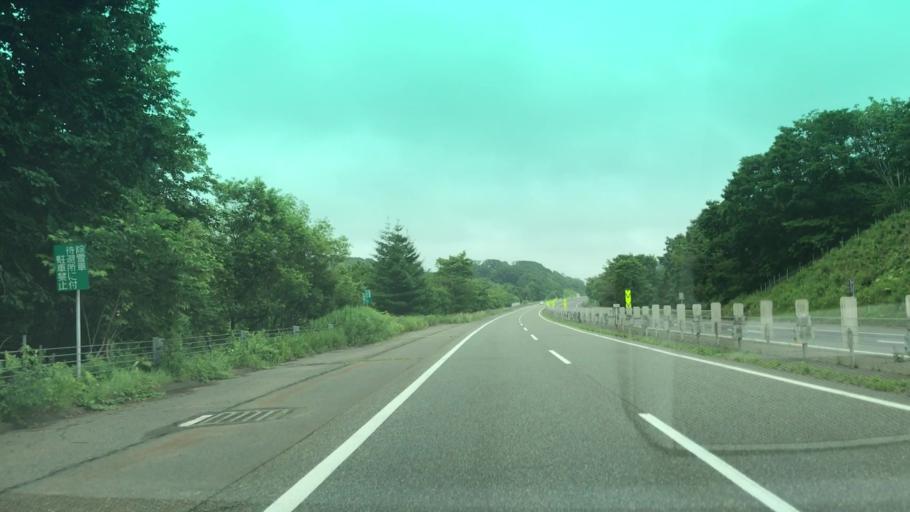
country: JP
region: Hokkaido
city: Tomakomai
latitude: 42.6506
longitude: 141.5446
